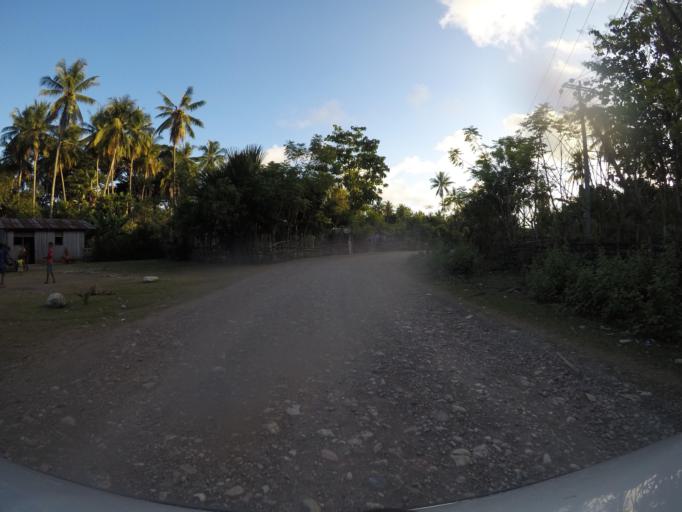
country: TL
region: Baucau
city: Venilale
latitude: -8.7458
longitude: 126.7132
